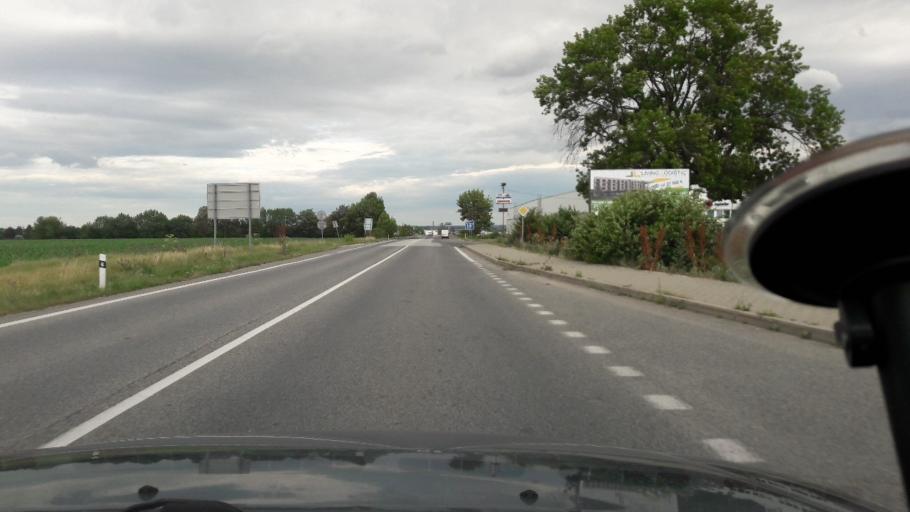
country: SK
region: Bratislavsky
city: Senec
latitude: 48.2399
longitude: 17.3622
